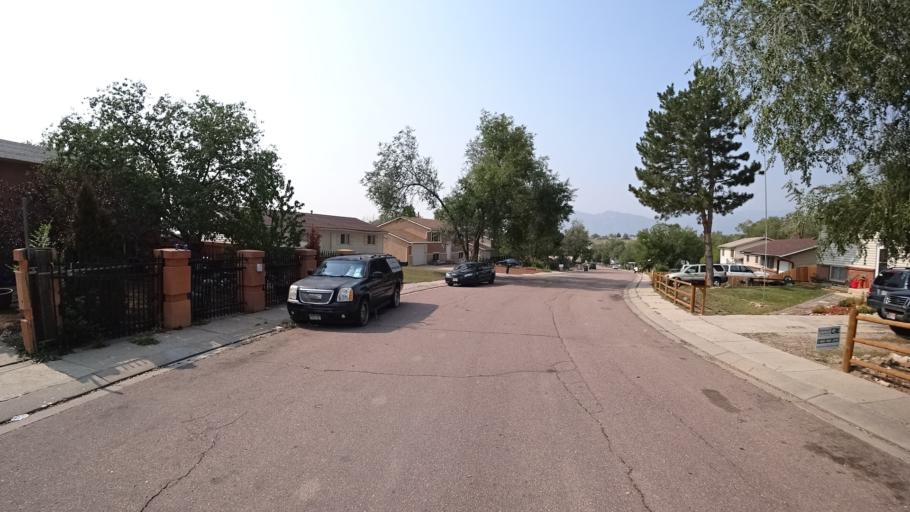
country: US
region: Colorado
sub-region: El Paso County
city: Stratmoor
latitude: 38.8102
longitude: -104.7624
